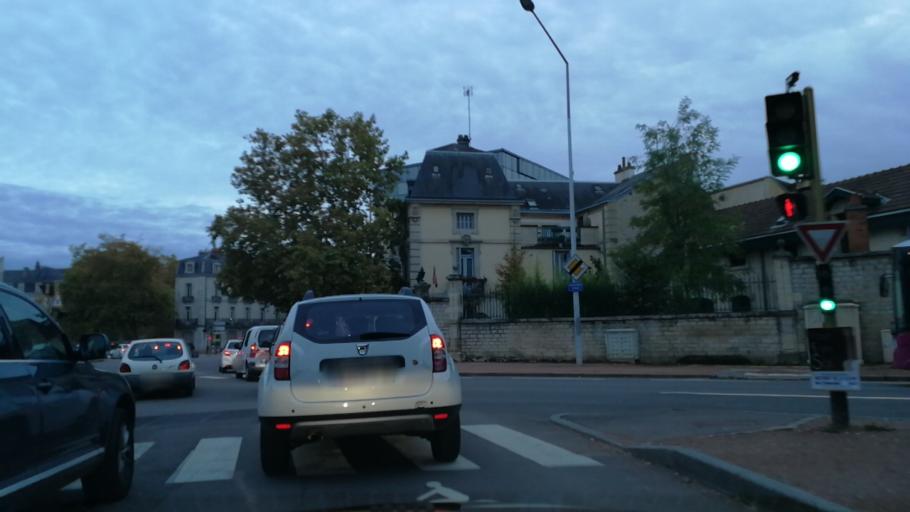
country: FR
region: Bourgogne
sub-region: Departement de la Cote-d'Or
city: Saint-Apollinaire
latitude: 47.3223
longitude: 5.0517
